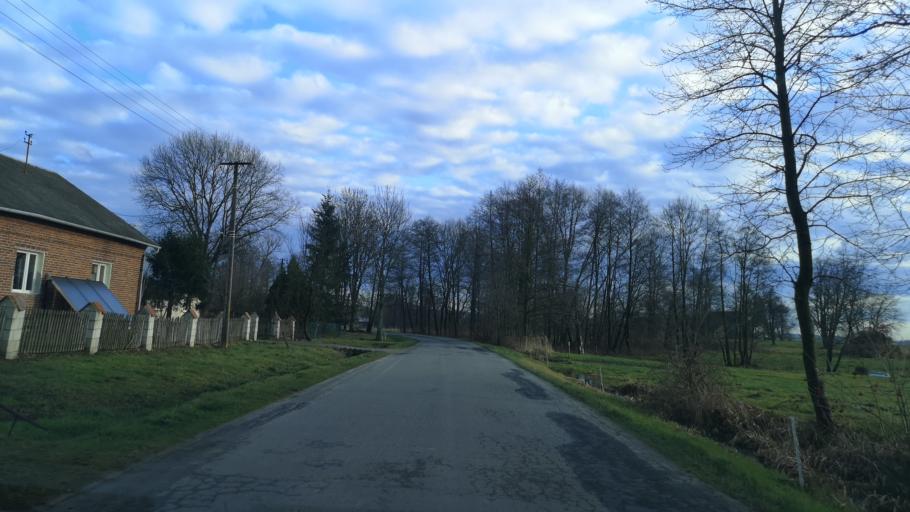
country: PL
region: Subcarpathian Voivodeship
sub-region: Powiat lezajski
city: Piskorowice
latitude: 50.2576
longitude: 22.5988
